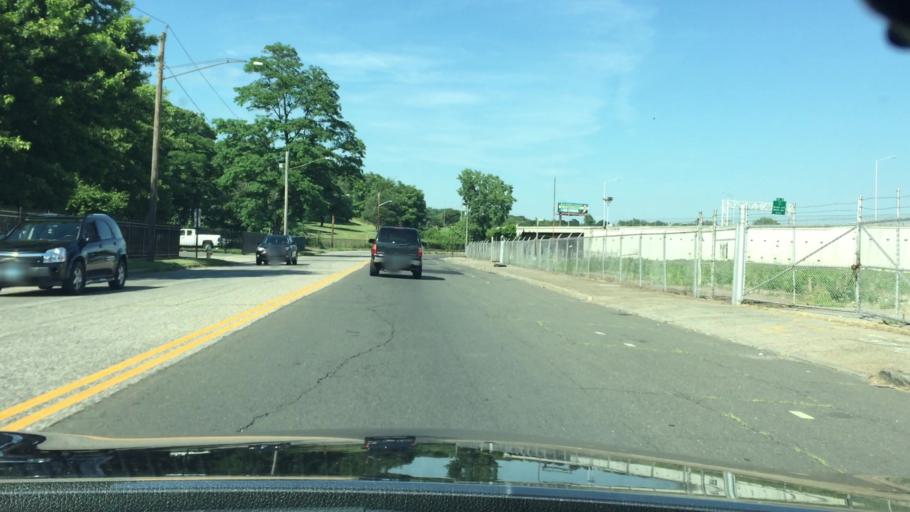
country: US
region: Connecticut
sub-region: Fairfield County
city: Bridgeport
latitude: 41.1994
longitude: -73.1957
